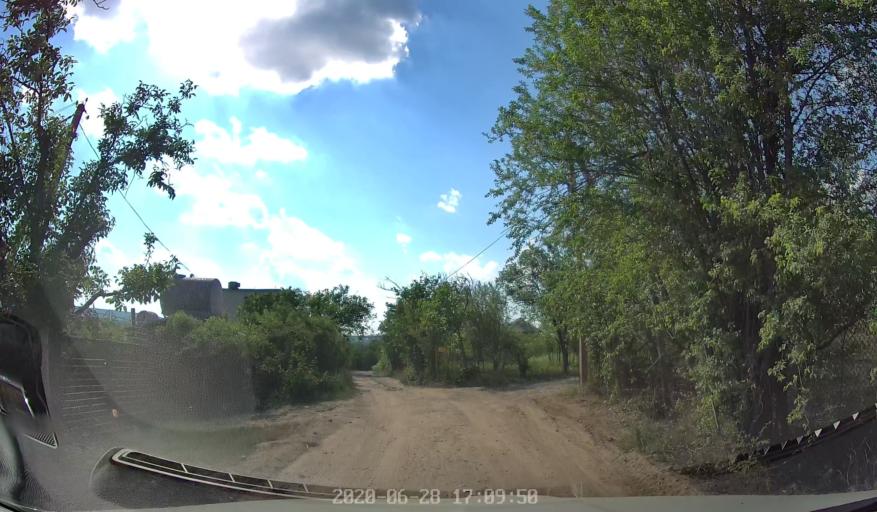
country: MD
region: Laloveni
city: Ialoveni
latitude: 46.9854
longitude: 28.7012
